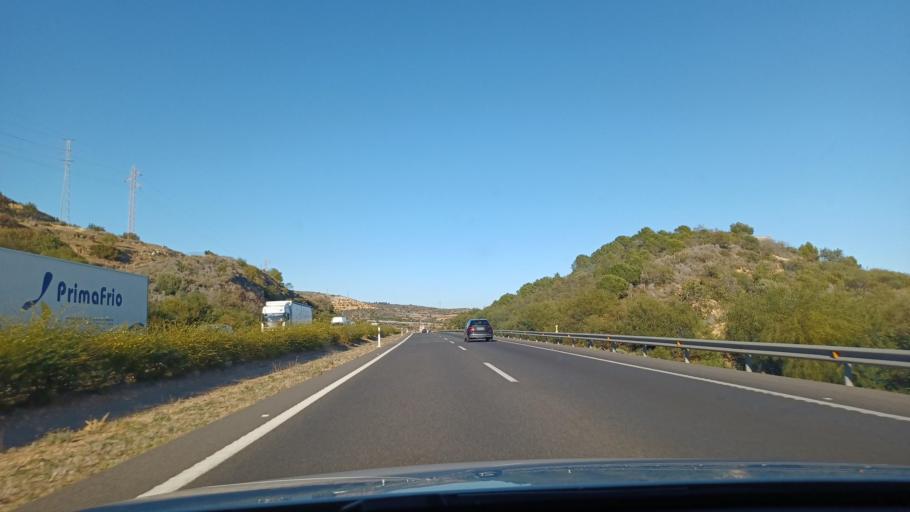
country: ES
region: Valencia
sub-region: Provincia de Castello
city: Torreblanca
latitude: 40.2164
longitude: 0.1846
